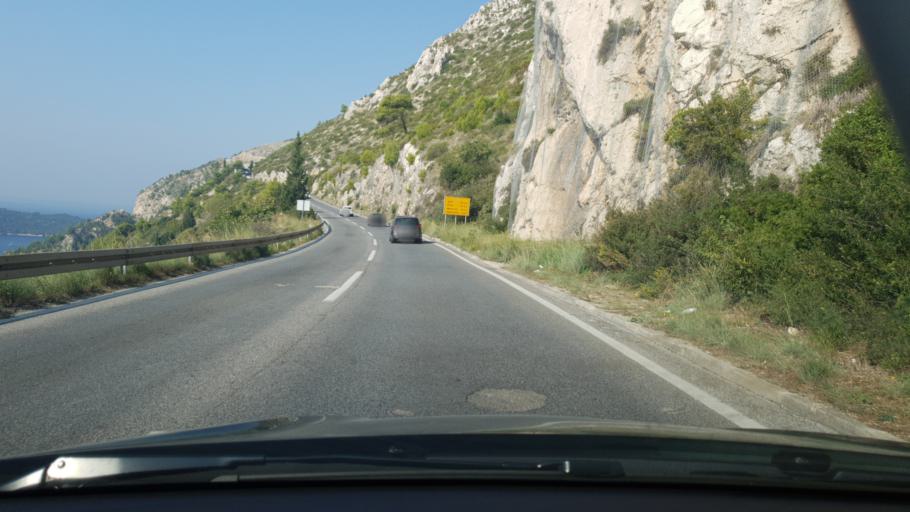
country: HR
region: Dubrovacko-Neretvanska
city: Cibaca
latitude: 42.6308
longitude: 18.1500
